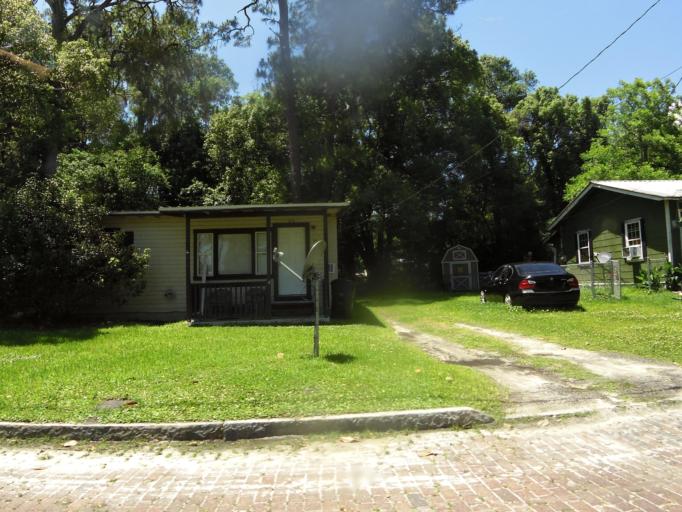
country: US
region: Florida
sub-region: Bradford County
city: Starke
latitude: 29.9471
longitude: -82.1067
